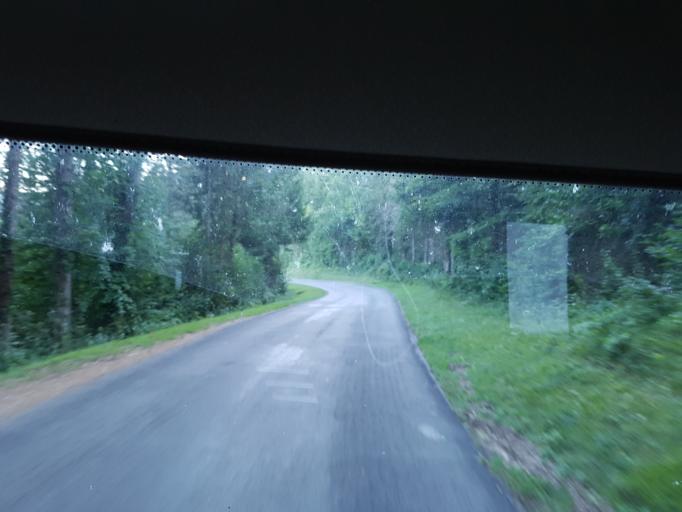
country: FR
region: Franche-Comte
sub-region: Departement du Jura
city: Orgelet
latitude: 46.4823
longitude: 5.6686
